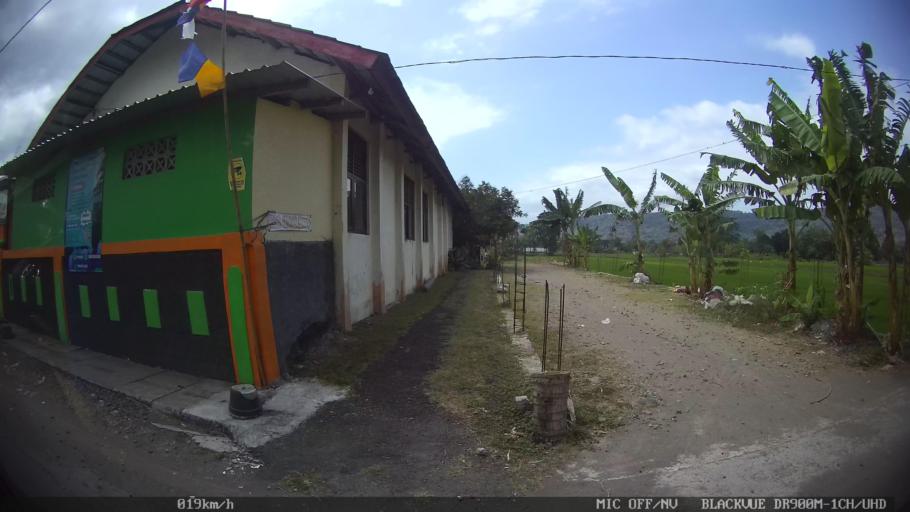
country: ID
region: Daerah Istimewa Yogyakarta
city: Depok
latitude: -7.8309
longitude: 110.4631
